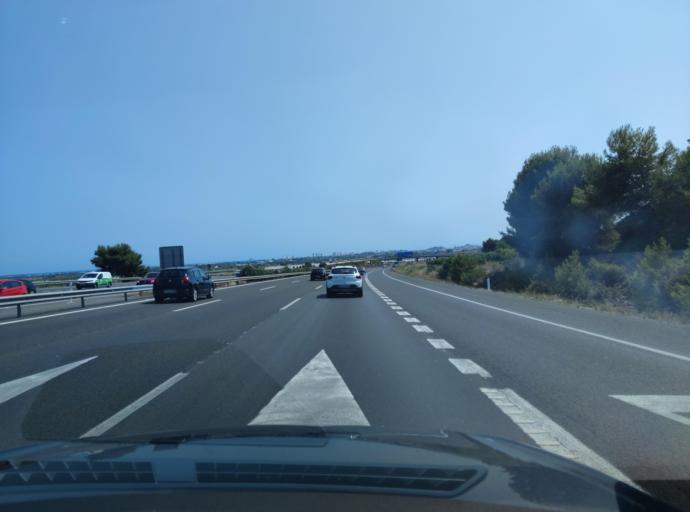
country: ES
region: Valencia
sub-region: Provincia de Valencia
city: Pucol
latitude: 39.6476
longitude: -0.3005
